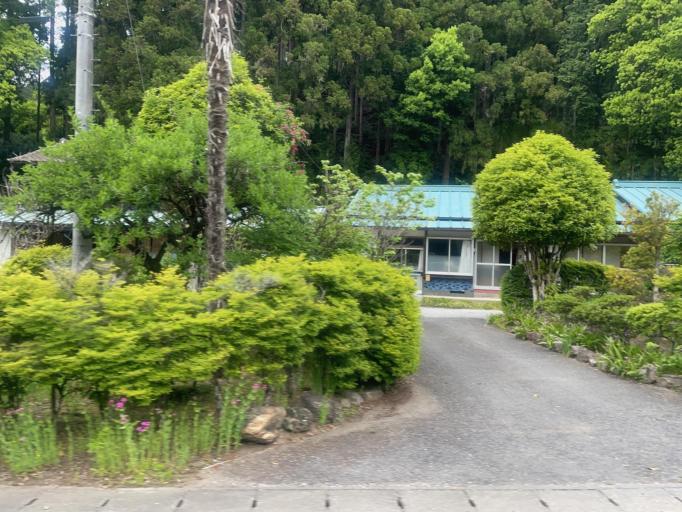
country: JP
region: Tochigi
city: Tanuma
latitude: 36.4745
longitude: 139.6267
